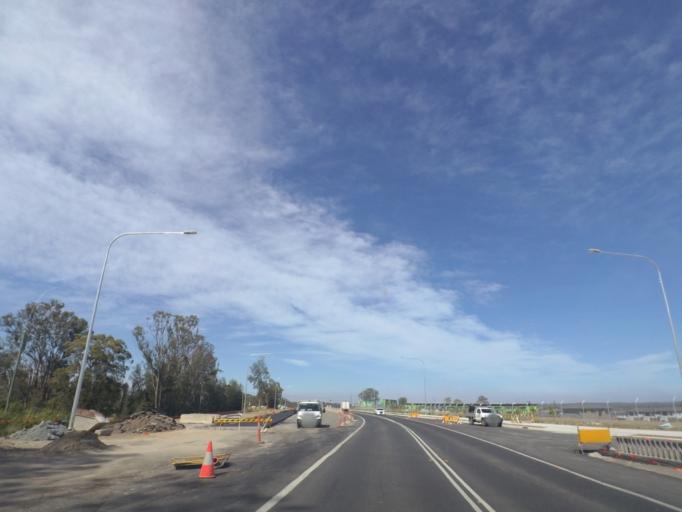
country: AU
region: New South Wales
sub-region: Campbelltown Municipality
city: Denham Court
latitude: -33.9755
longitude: 150.8541
